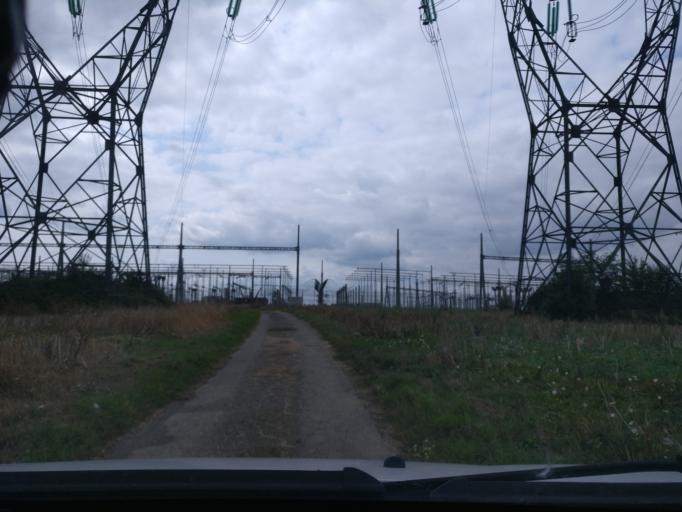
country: FR
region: Brittany
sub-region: Departement d'Ille-et-Vilaine
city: Noyal-sur-Vilaine
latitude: 48.0930
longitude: -1.5528
